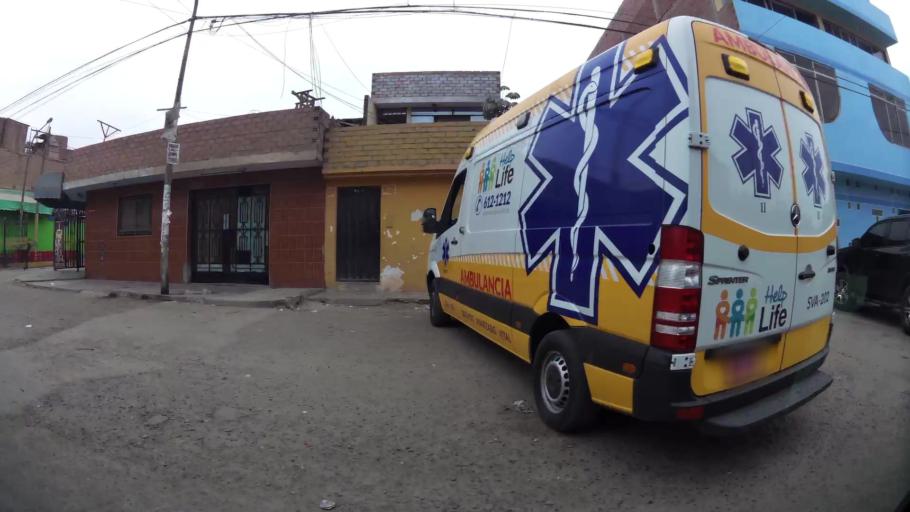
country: PE
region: Lima
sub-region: Lima
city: Independencia
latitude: -11.9473
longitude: -77.0915
